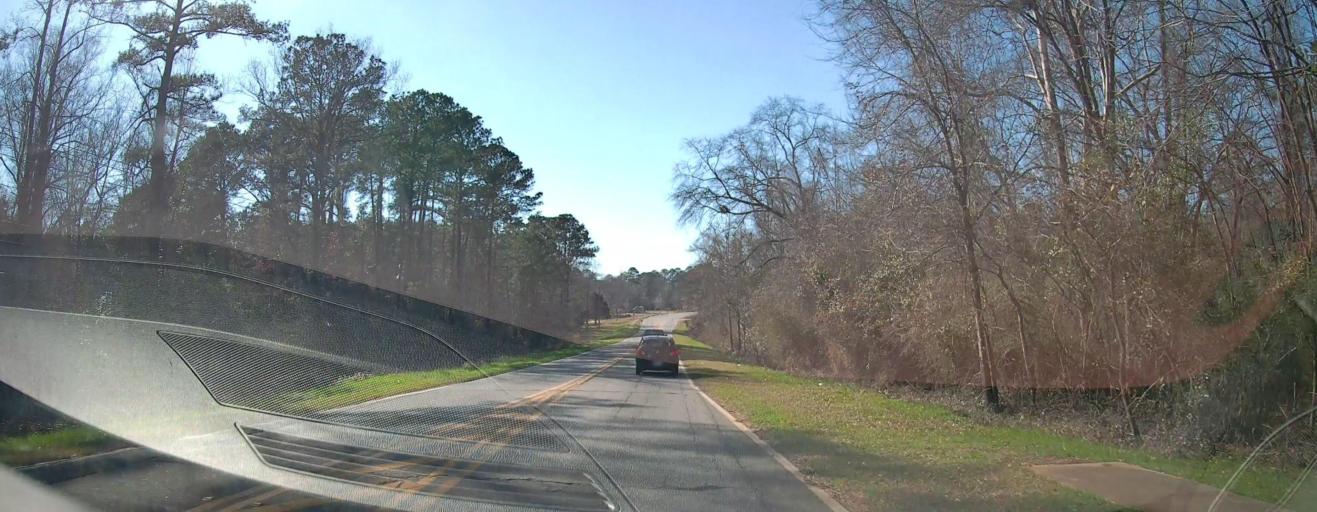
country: US
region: Georgia
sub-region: Sumter County
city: Americus
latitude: 32.0599
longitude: -84.2070
